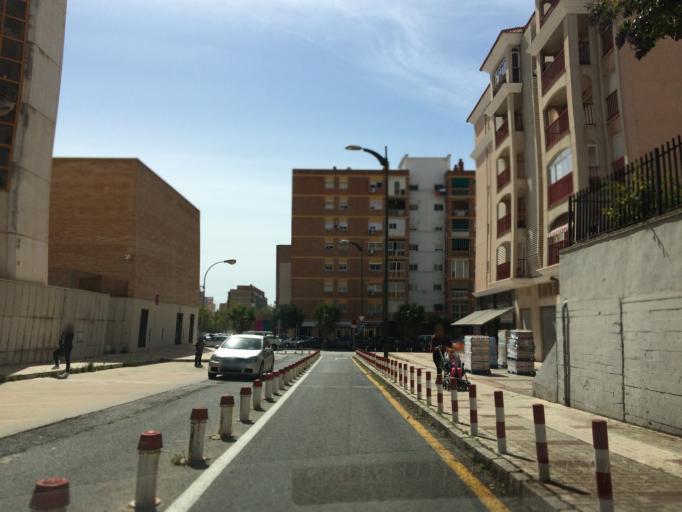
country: ES
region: Andalusia
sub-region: Provincia de Malaga
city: Malaga
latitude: 36.7142
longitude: -4.4493
